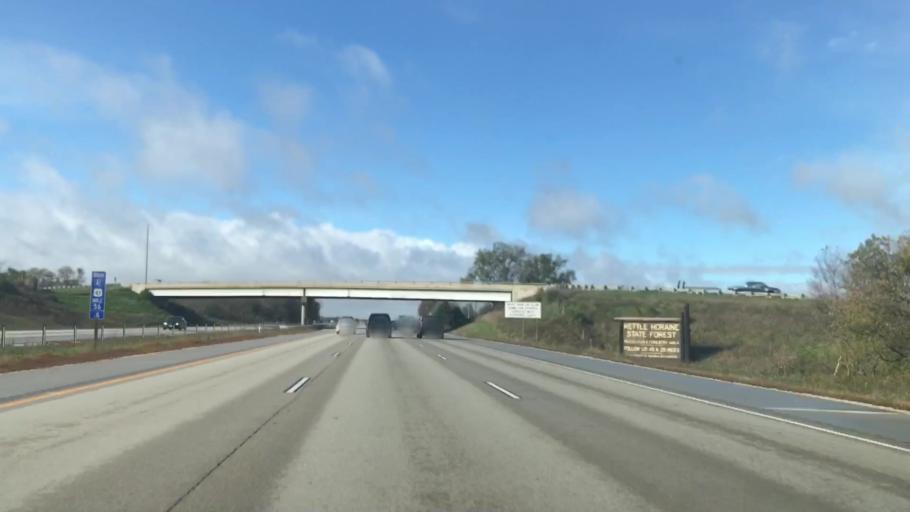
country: US
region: Wisconsin
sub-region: Washington County
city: Richfield
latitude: 43.2353
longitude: -88.1723
